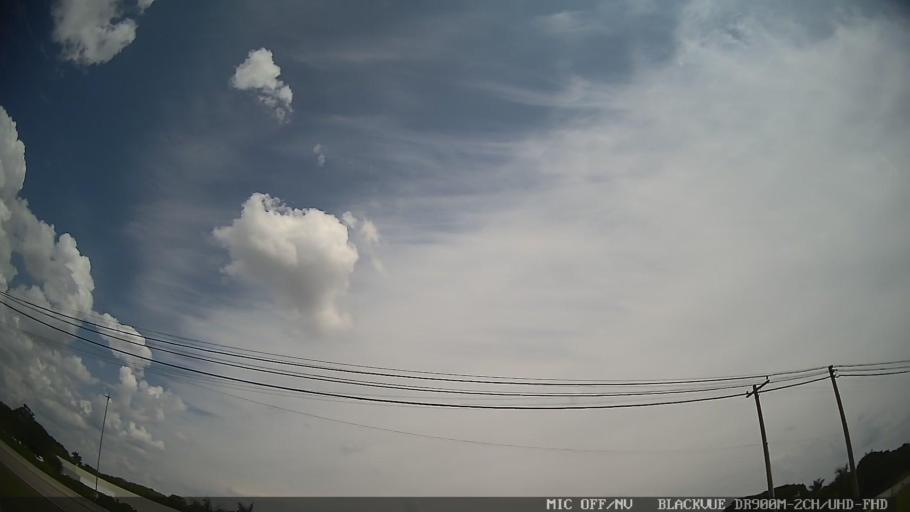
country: BR
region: Sao Paulo
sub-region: Itatiba
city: Itatiba
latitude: -22.9723
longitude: -46.7220
